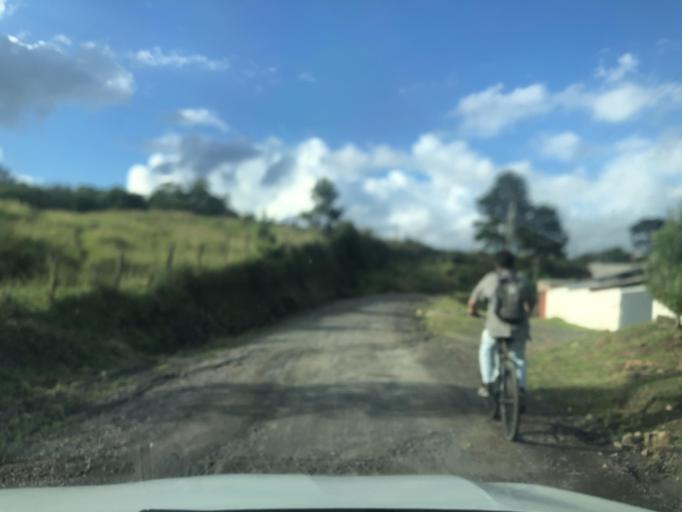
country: BR
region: Santa Catarina
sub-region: Lages
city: Lages
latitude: -27.7940
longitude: -50.3171
